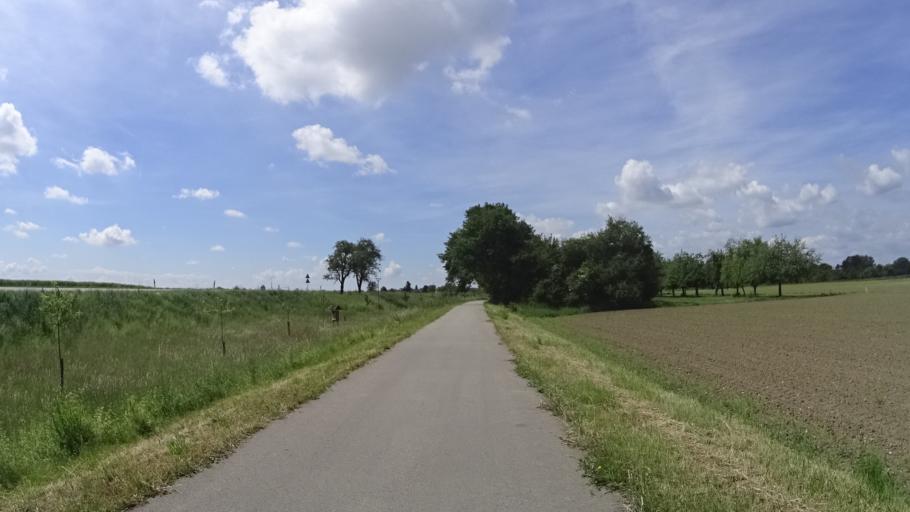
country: DE
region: Baden-Wuerttemberg
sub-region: Freiburg Region
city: Meissenheim
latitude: 48.3962
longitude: 7.7663
